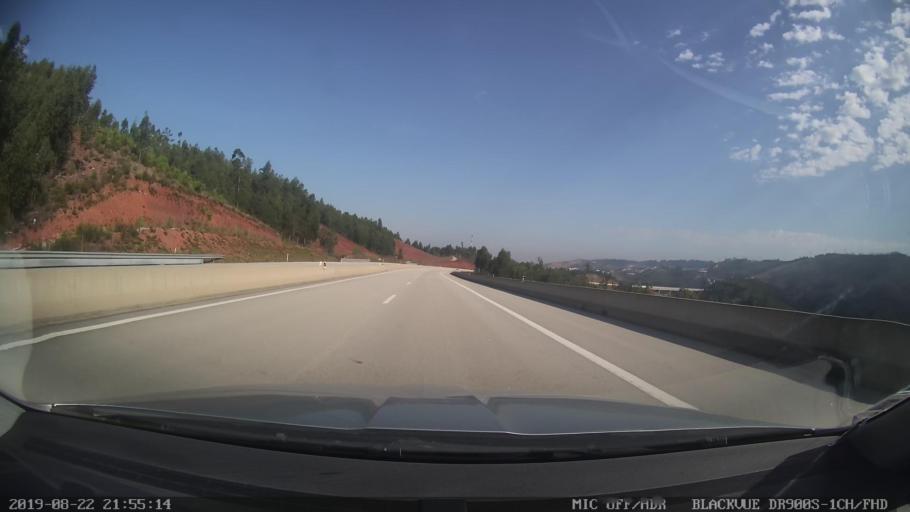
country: PT
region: Coimbra
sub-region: Coimbra
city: Coimbra
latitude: 40.1501
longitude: -8.3840
